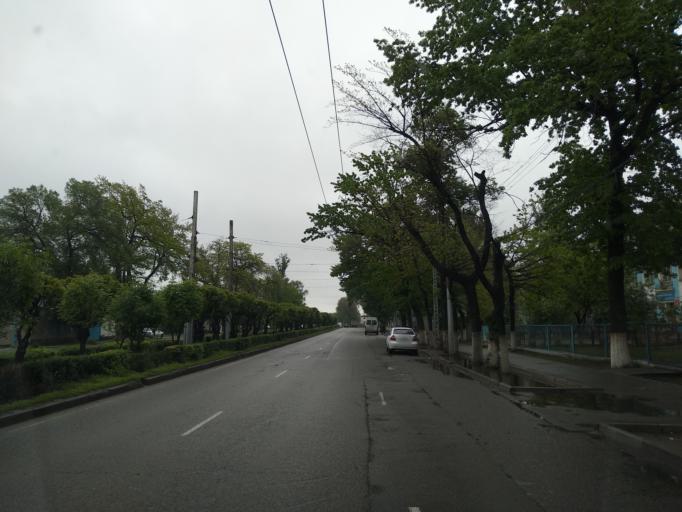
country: KG
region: Chuy
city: Bishkek
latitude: 42.8850
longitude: 74.6173
